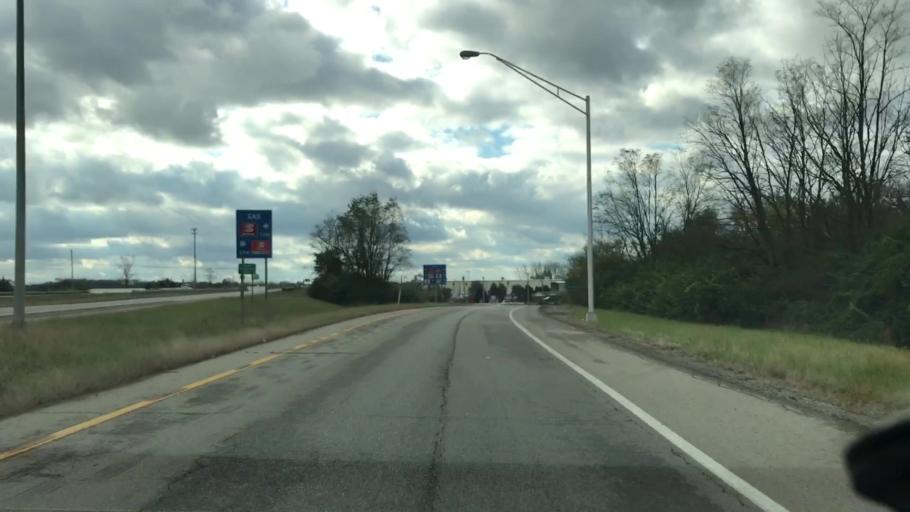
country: US
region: Ohio
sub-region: Clark County
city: Holiday Valley
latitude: 39.8473
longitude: -83.9942
